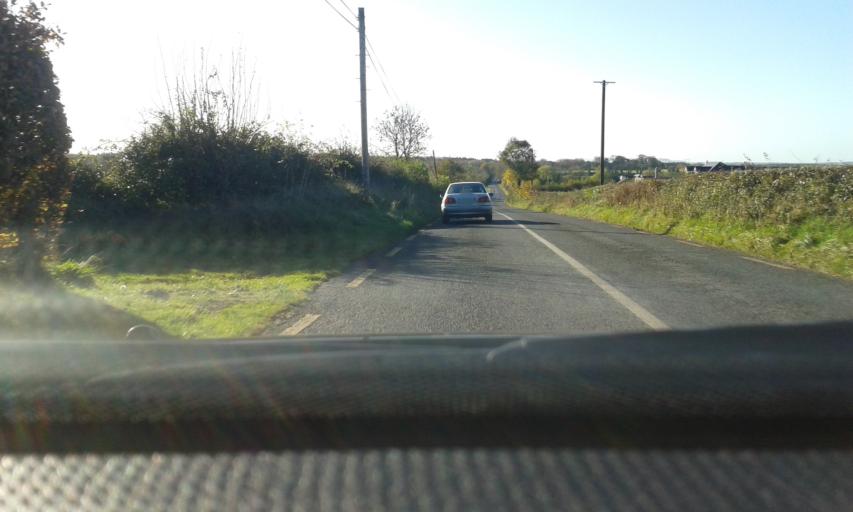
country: IE
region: Leinster
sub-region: Kildare
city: Rathangan
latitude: 53.2004
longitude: -7.0033
